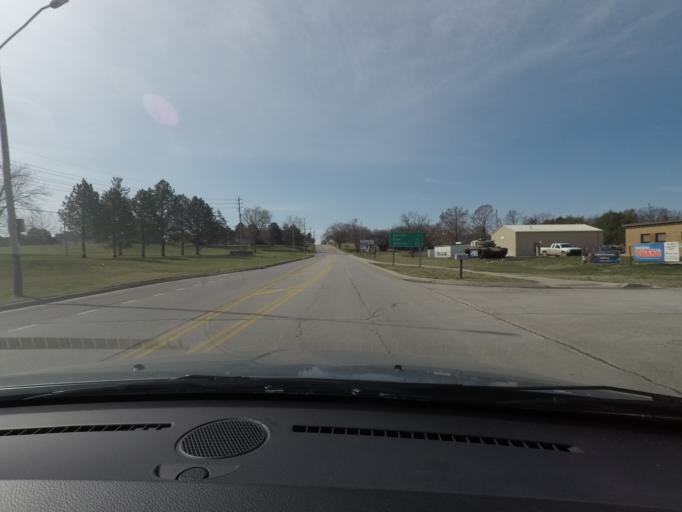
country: US
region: Kansas
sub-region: Lyon County
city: Emporia
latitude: 38.4208
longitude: -96.1818
